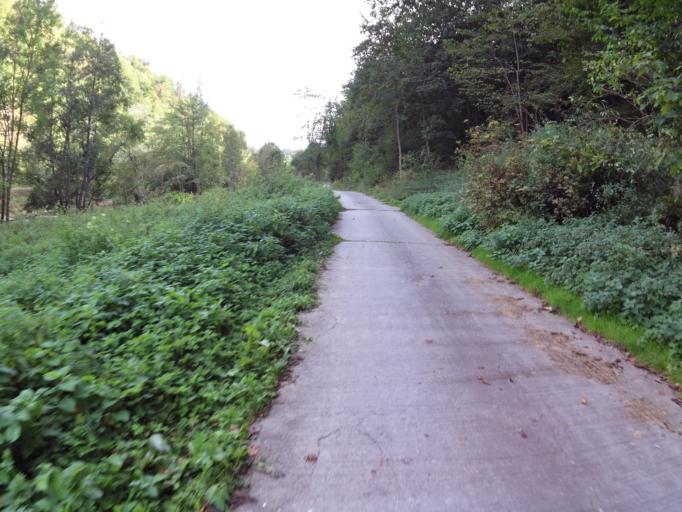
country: DE
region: Baden-Wuerttemberg
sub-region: Freiburg Region
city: Villingendorf
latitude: 48.2029
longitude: 8.6123
